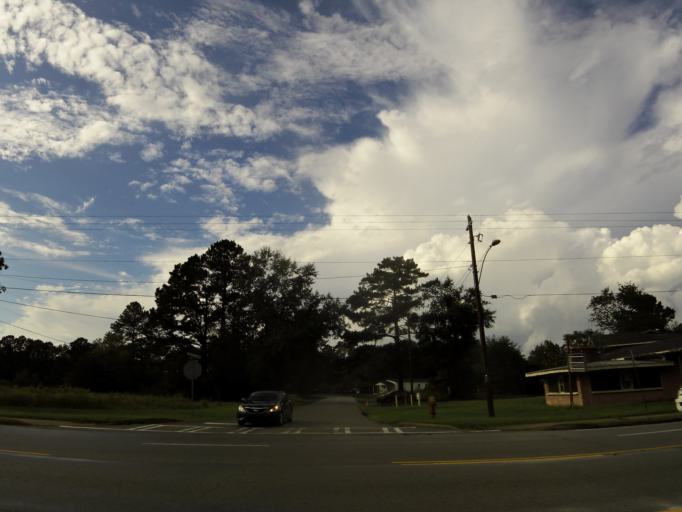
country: US
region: Georgia
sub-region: Liberty County
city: Walthourville
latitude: 31.7816
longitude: -81.6182
